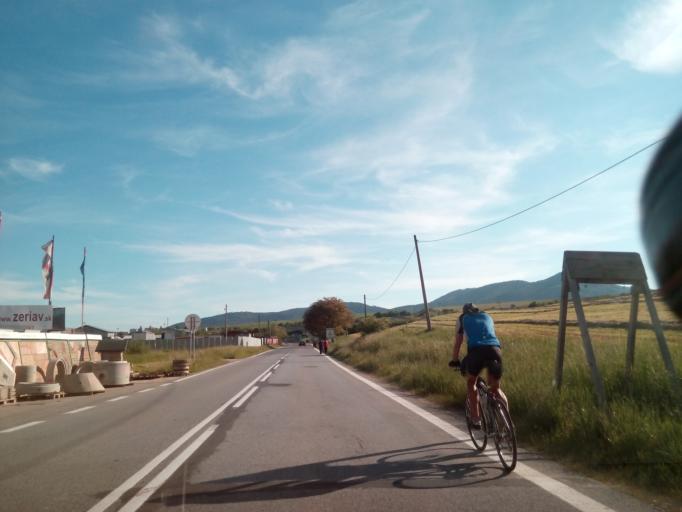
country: SK
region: Kosicky
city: Krompachy
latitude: 49.0124
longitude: 20.9450
